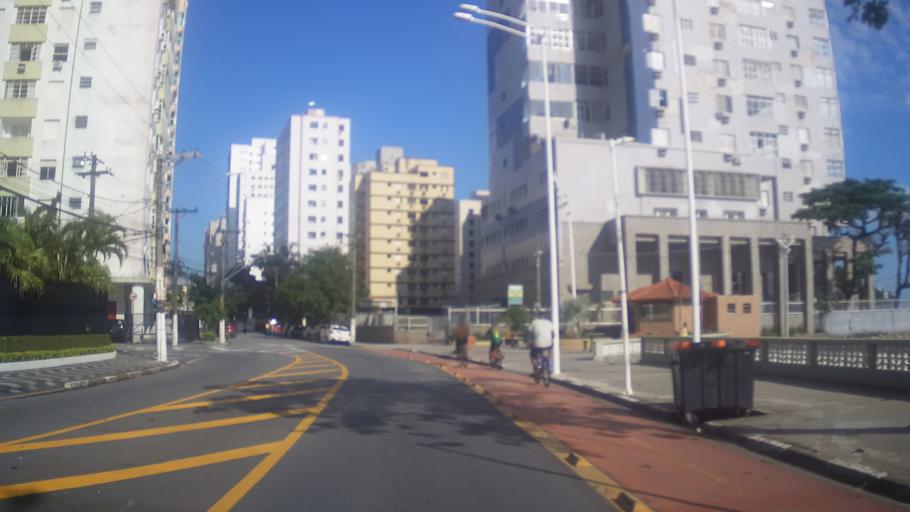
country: BR
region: Sao Paulo
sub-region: Sao Vicente
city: Sao Vicente
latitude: -23.9708
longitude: -46.3739
